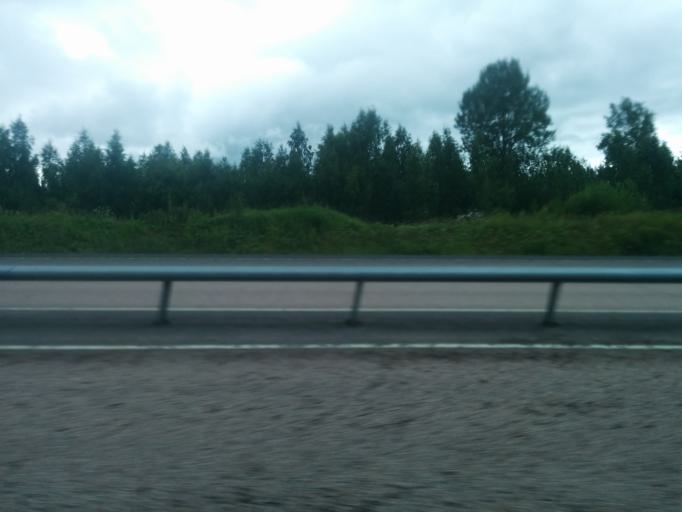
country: FI
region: Pirkanmaa
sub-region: Tampere
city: Orivesi
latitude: 61.7065
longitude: 24.5448
